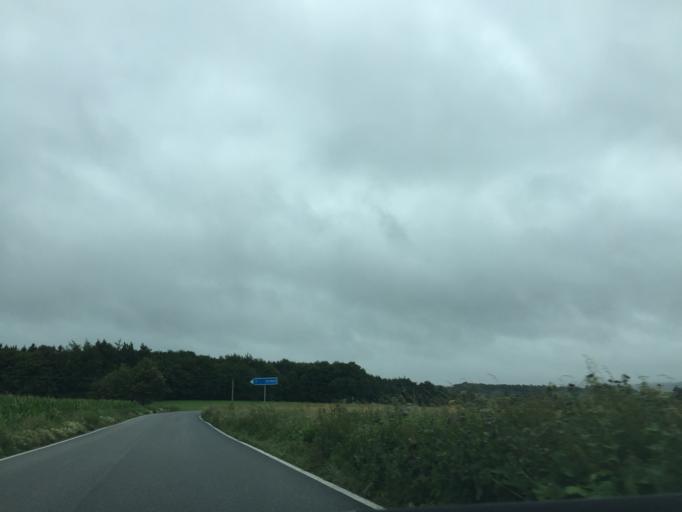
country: CZ
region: South Moravian
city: Ostrov u Macochy
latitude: 49.4020
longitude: 16.7469
